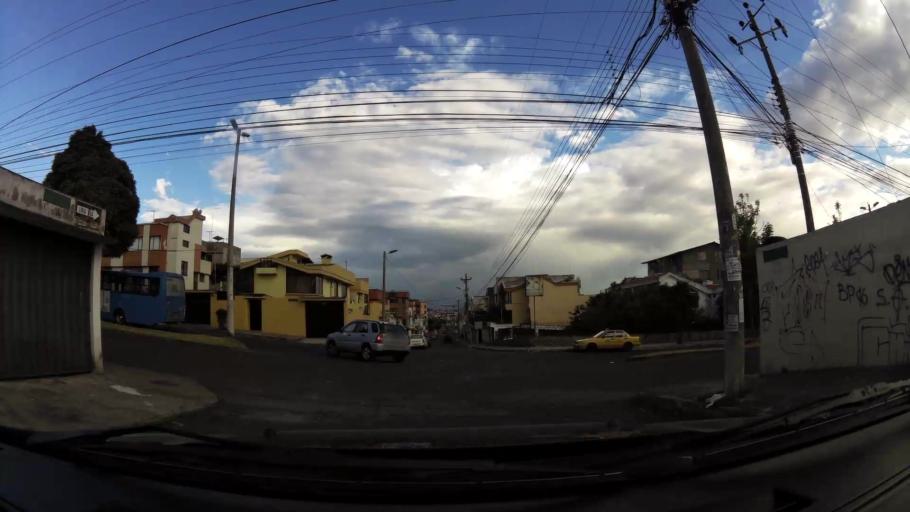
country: EC
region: Pichincha
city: Quito
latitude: -0.1428
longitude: -78.4816
